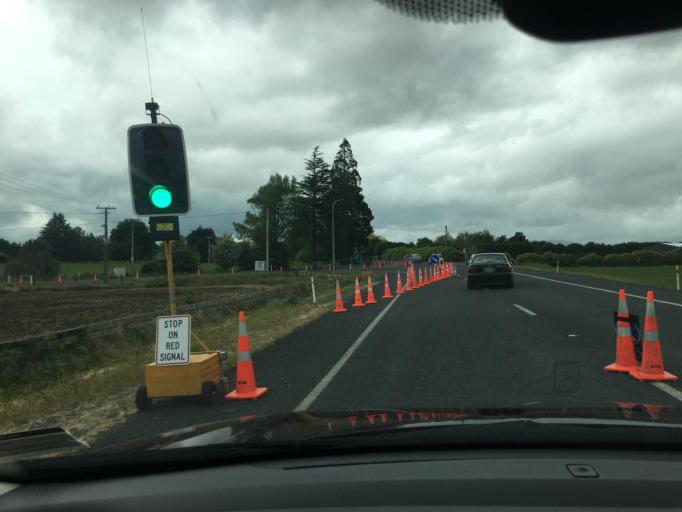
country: NZ
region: Waikato
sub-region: Waipa District
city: Cambridge
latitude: -37.9248
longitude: 175.4339
